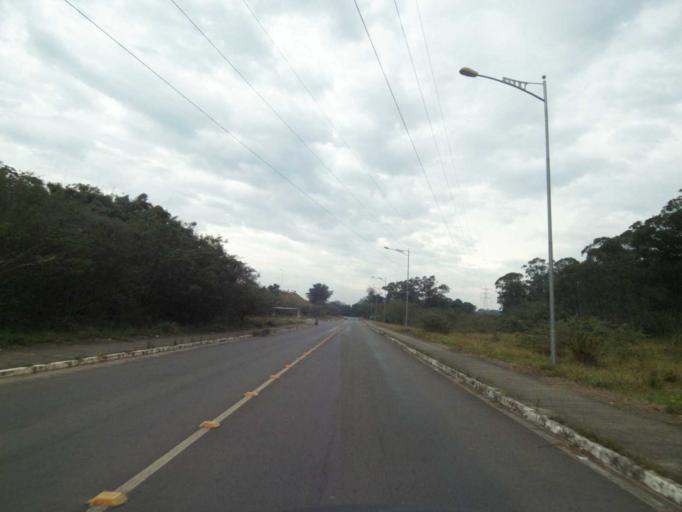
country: BR
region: Rio Grande do Sul
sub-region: Sao Leopoldo
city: Sao Leopoldo
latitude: -29.7859
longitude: -51.1651
